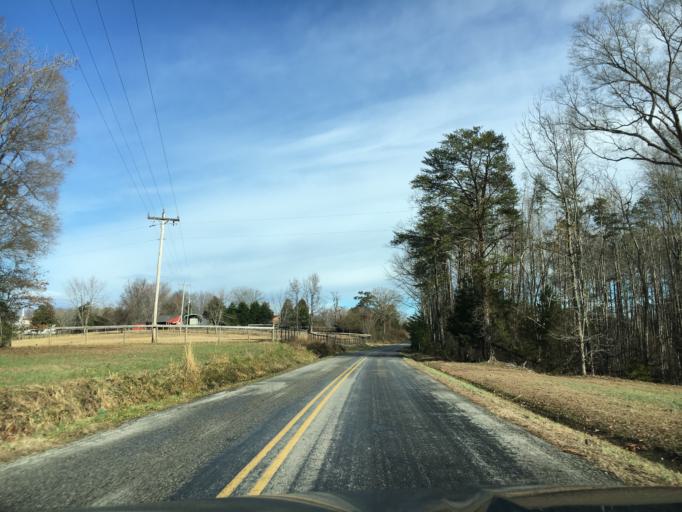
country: US
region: Virginia
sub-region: Nottoway County
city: Crewe
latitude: 37.3261
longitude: -78.1698
